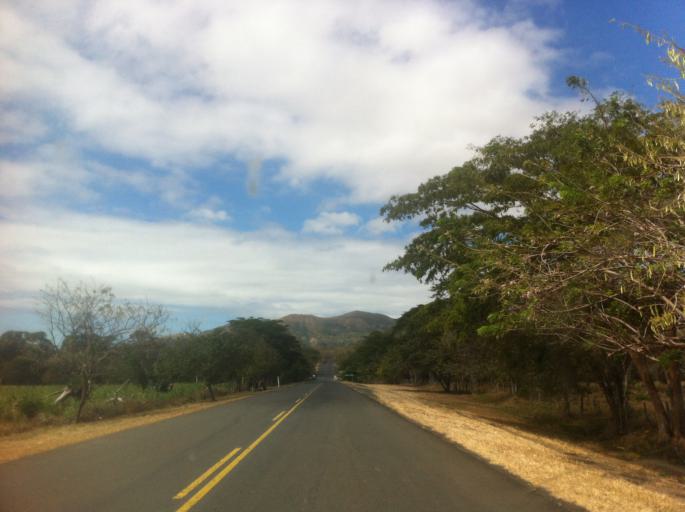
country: NI
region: Chontales
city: Acoyapa
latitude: 12.0035
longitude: -85.1818
